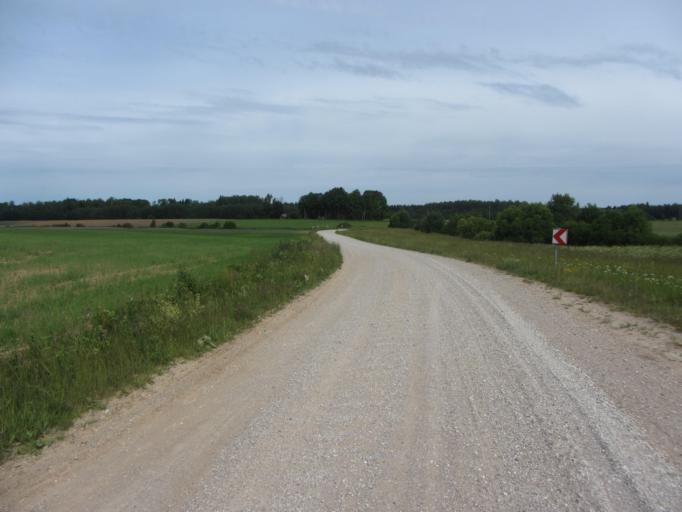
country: LT
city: Obeliai
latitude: 56.0501
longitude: 25.2222
